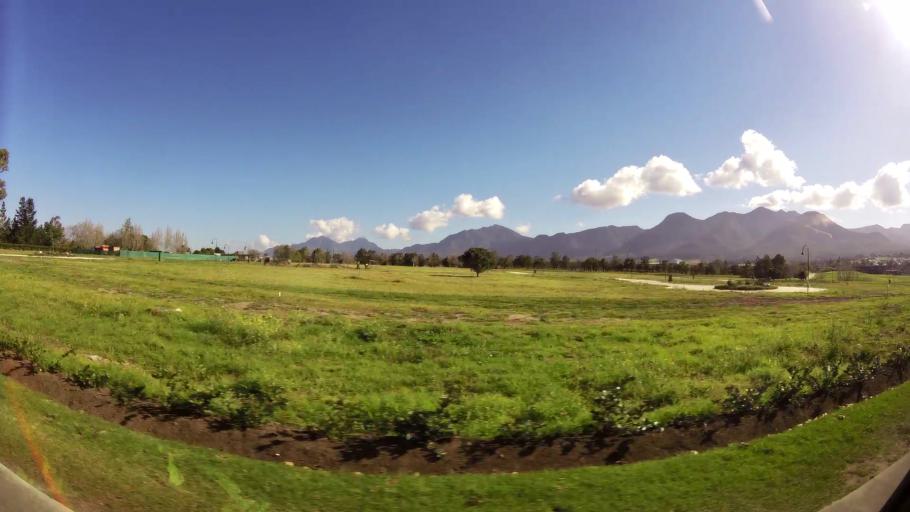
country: ZA
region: Western Cape
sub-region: Eden District Municipality
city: George
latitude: -33.9623
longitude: 22.4021
